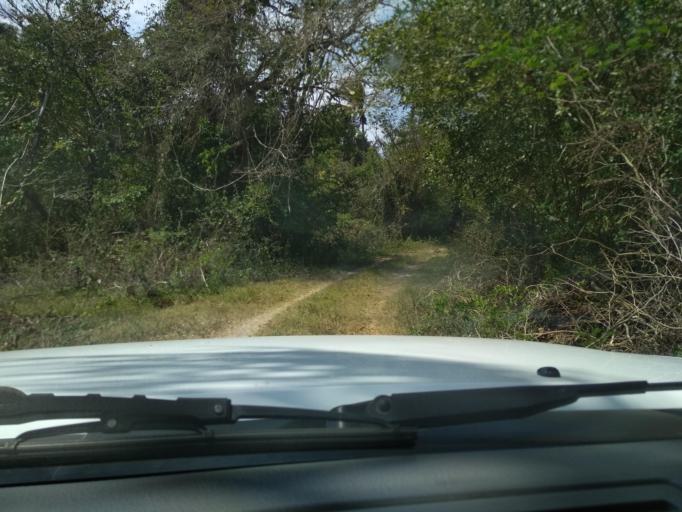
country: MX
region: Veracruz
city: Manlio Fabio Altamirano
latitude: 19.1592
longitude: -96.3305
